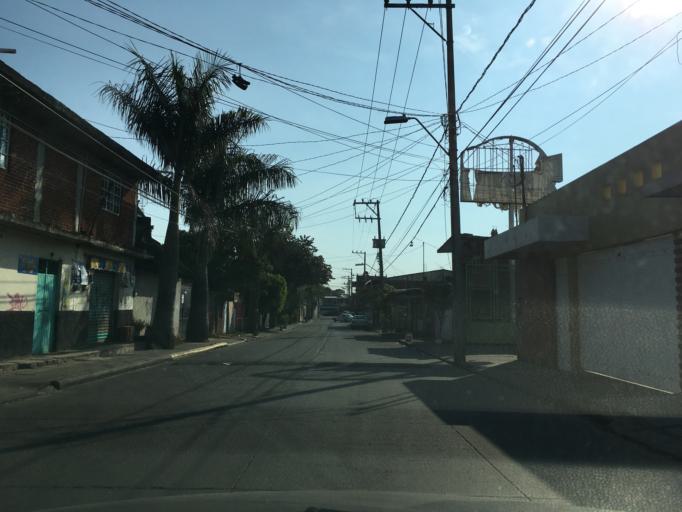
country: MX
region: Michoacan
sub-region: Uruapan
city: Uruapan
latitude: 19.4065
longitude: -102.0686
